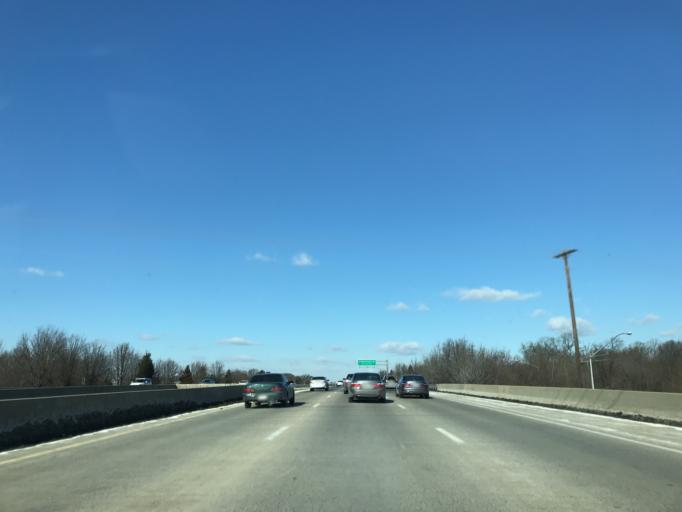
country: US
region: Maryland
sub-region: Prince George's County
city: Camp Springs
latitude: 38.8045
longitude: -76.9054
